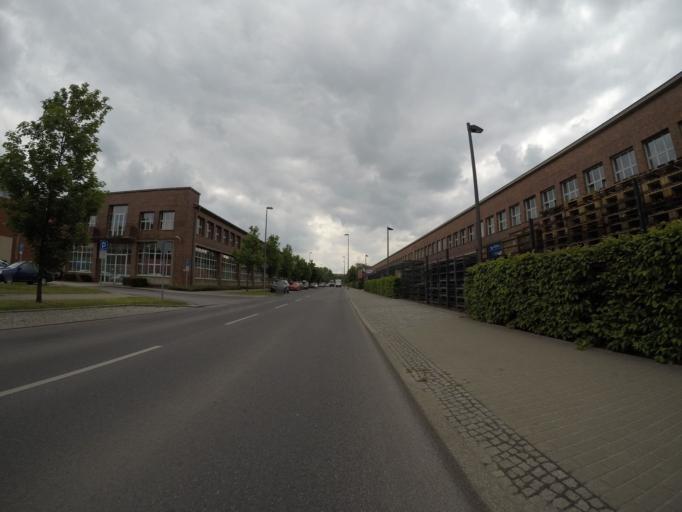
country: DE
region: Berlin
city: Falkenberg
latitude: 52.5429
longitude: 13.5361
